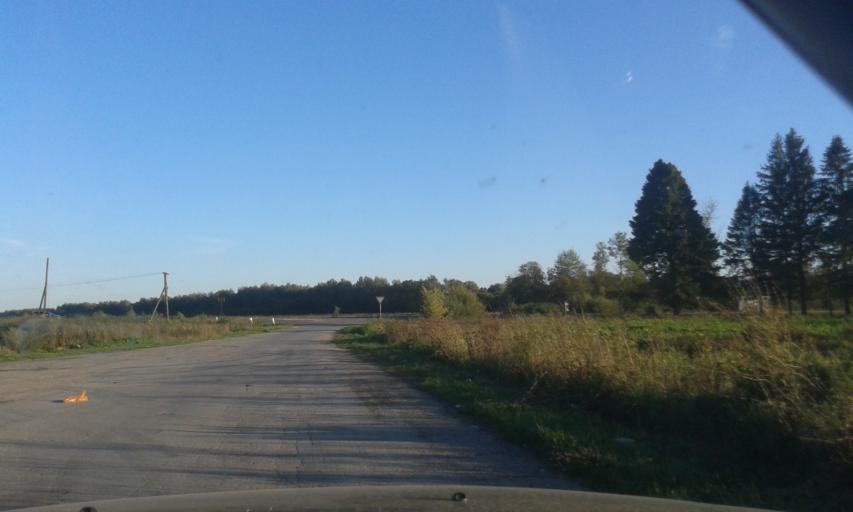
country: RU
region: Tula
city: Krapivna
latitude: 54.1151
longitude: 37.1527
